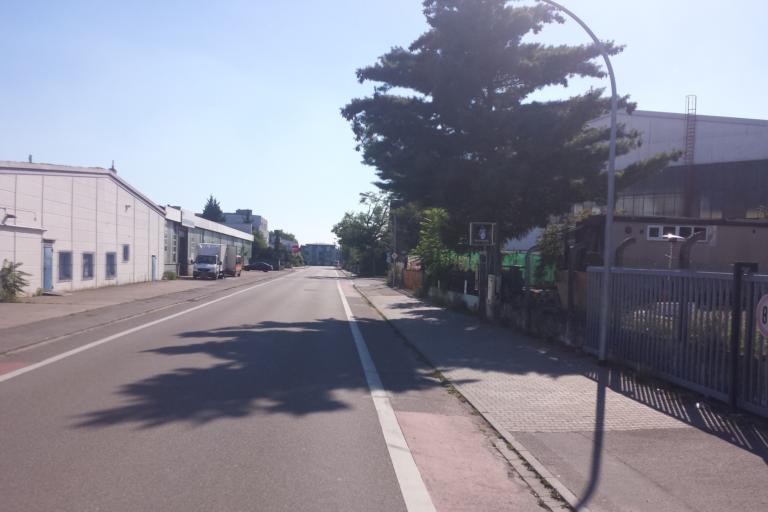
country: DE
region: Hesse
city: Viernheim
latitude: 49.5466
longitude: 8.5909
